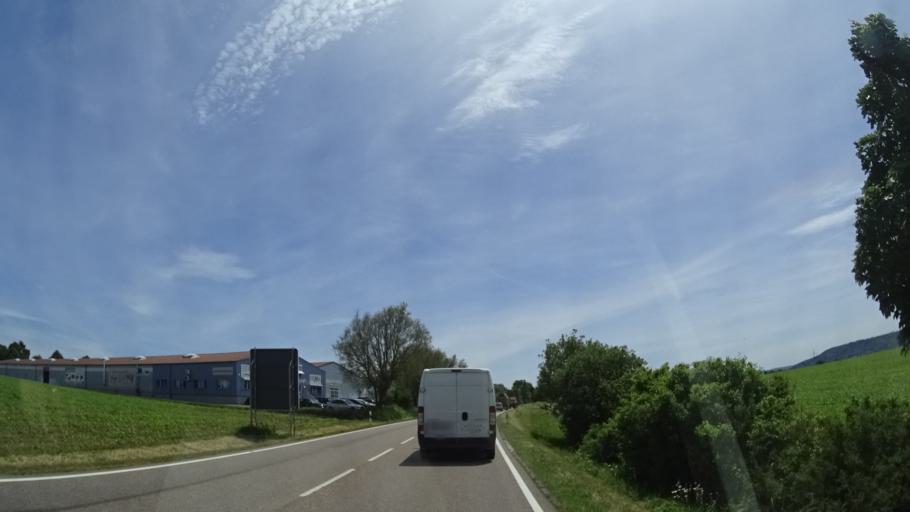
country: DE
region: Baden-Wuerttemberg
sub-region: Regierungsbezirk Stuttgart
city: Untermunkheim
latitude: 49.1755
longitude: 9.7114
